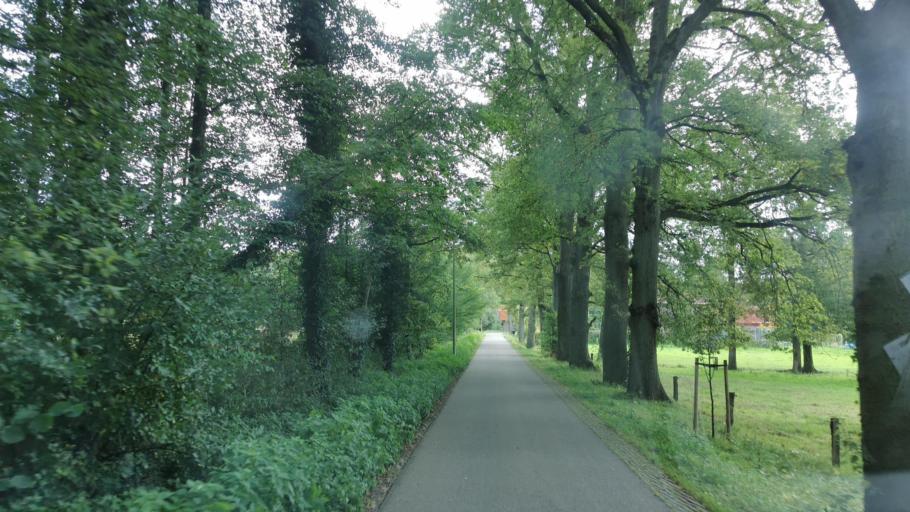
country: NL
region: Overijssel
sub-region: Gemeente Oldenzaal
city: Oldenzaal
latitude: 52.3097
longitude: 6.9480
